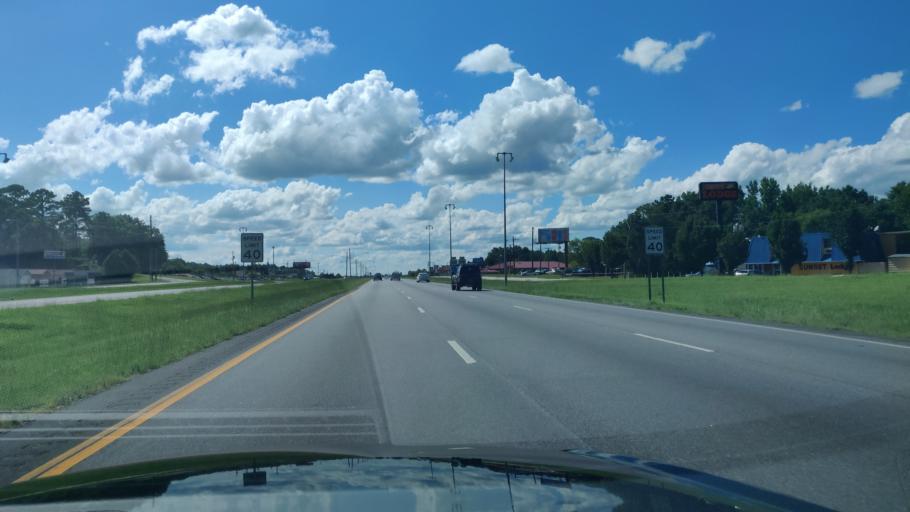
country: US
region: Alabama
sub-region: Russell County
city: Phenix City
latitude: 32.4574
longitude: -85.0129
